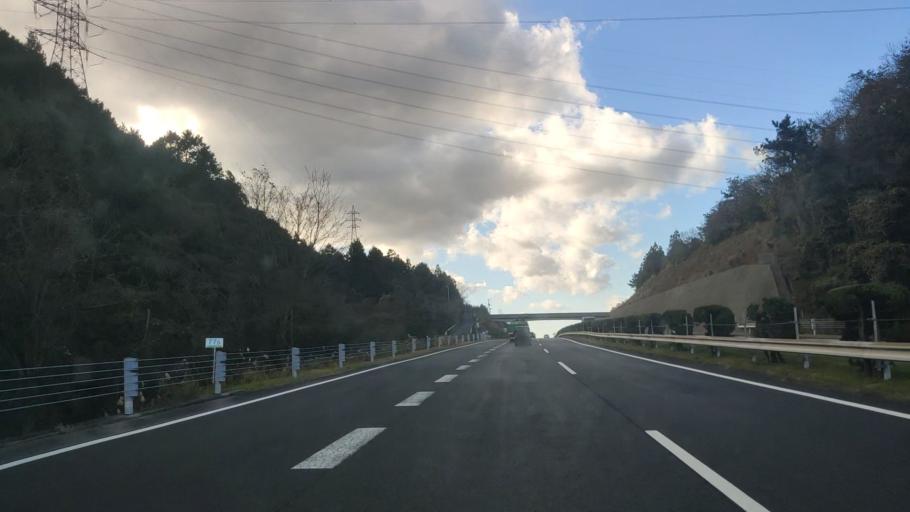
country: JP
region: Ehime
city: Niihama
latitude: 33.9417
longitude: 133.3966
